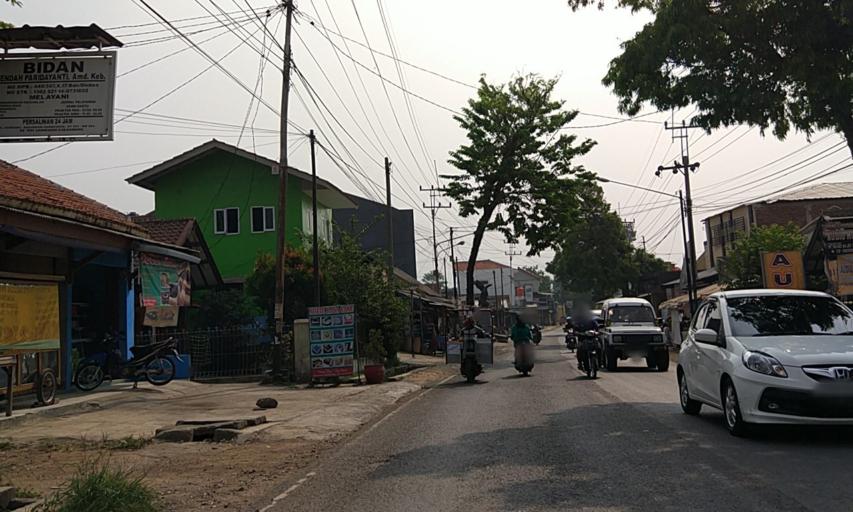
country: ID
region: West Java
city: Banjaran
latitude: -7.0435
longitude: 107.5561
